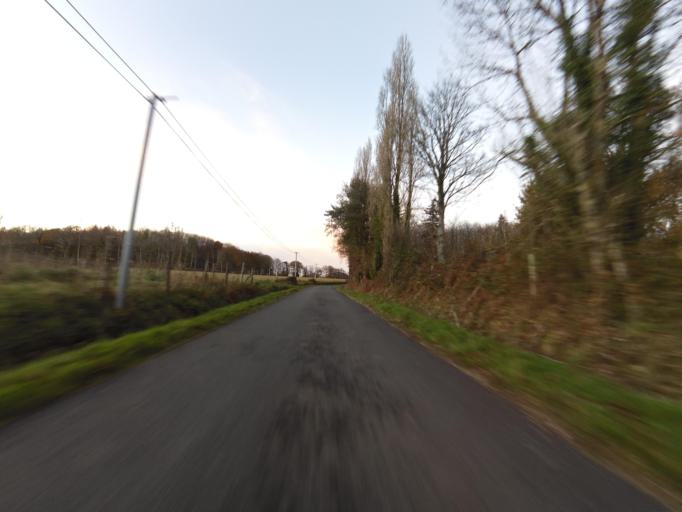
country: FR
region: Brittany
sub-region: Departement du Morbihan
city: Pluherlin
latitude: 47.7227
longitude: -2.3662
